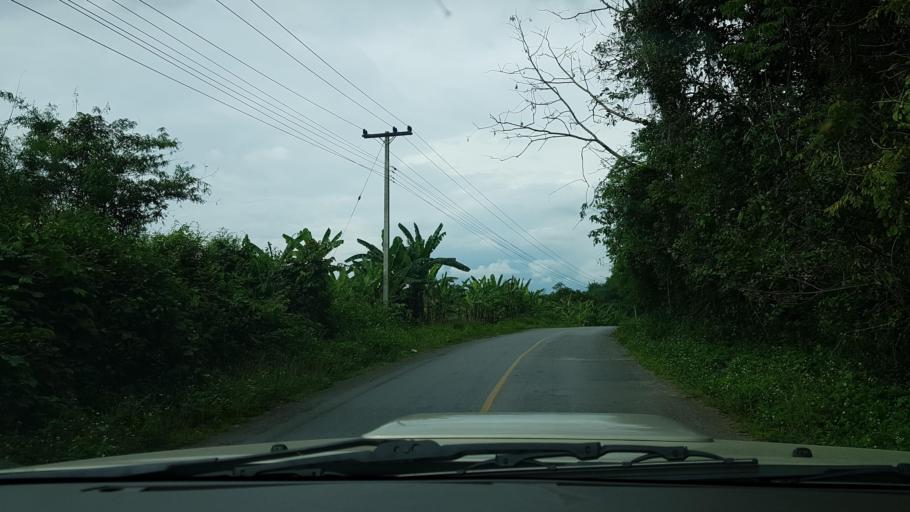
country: LA
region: Loungnamtha
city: Muang Nale
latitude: 20.3774
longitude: 101.7380
